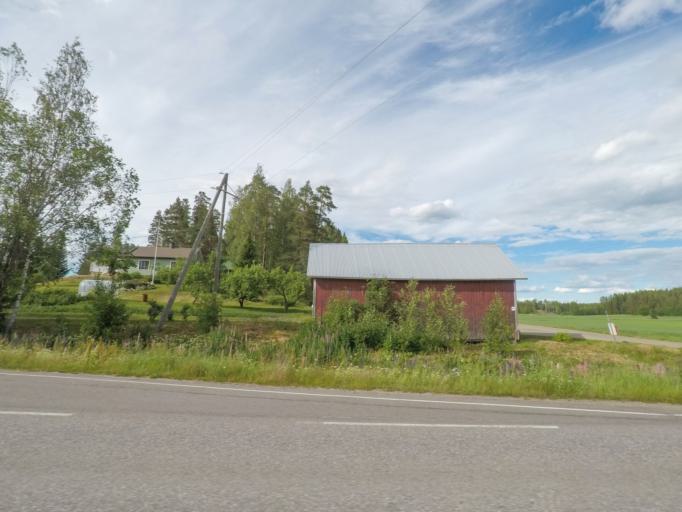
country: FI
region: Uusimaa
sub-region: Porvoo
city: Pukkila
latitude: 60.7705
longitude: 25.4589
